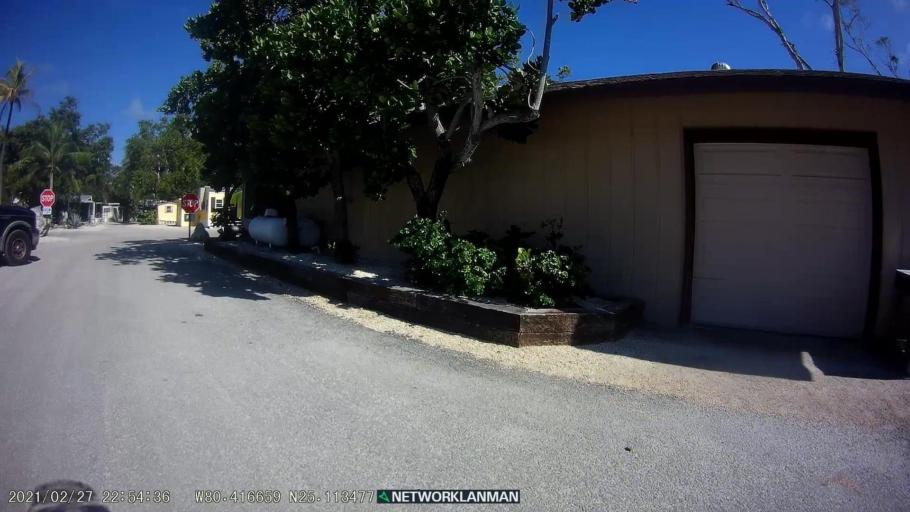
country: US
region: Florida
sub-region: Monroe County
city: Key Largo
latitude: 25.1140
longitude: -80.4166
